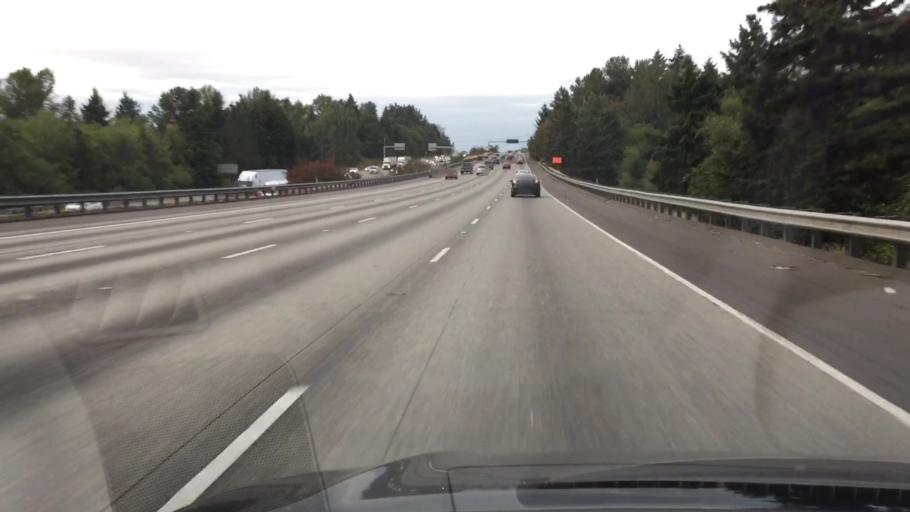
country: US
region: Washington
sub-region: King County
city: Lakeland North
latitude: 47.3670
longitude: -122.2939
